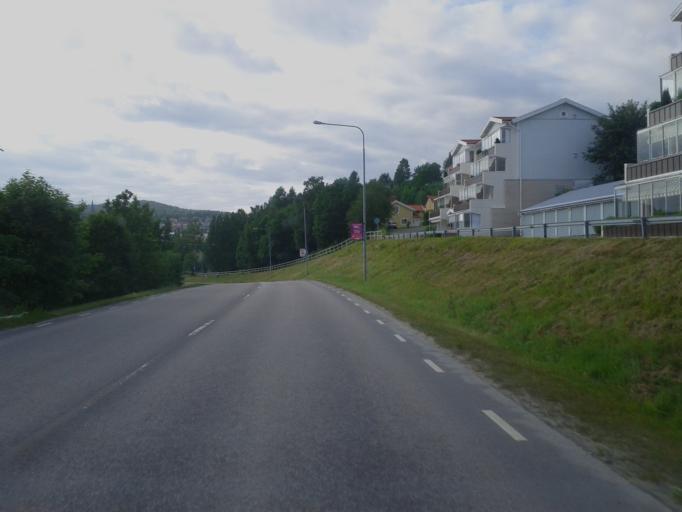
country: SE
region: Vaesternorrland
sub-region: OErnskoeldsviks Kommun
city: Ornskoldsvik
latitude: 63.2864
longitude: 18.7315
